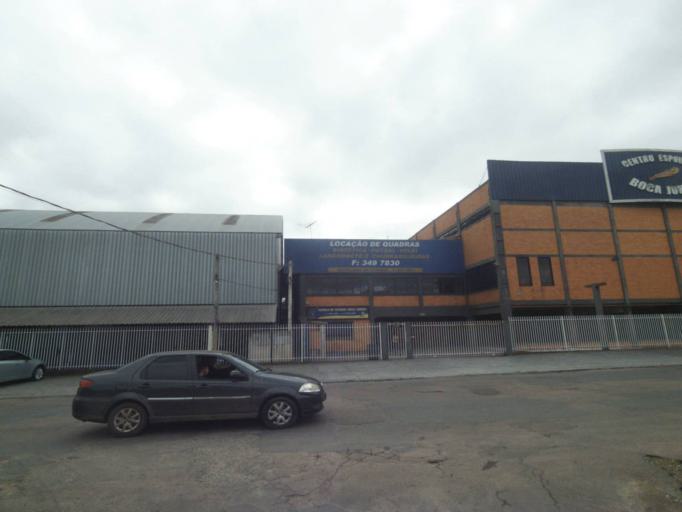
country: BR
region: Parana
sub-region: Sao Jose Dos Pinhais
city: Sao Jose dos Pinhais
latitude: -25.5363
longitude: -49.2961
